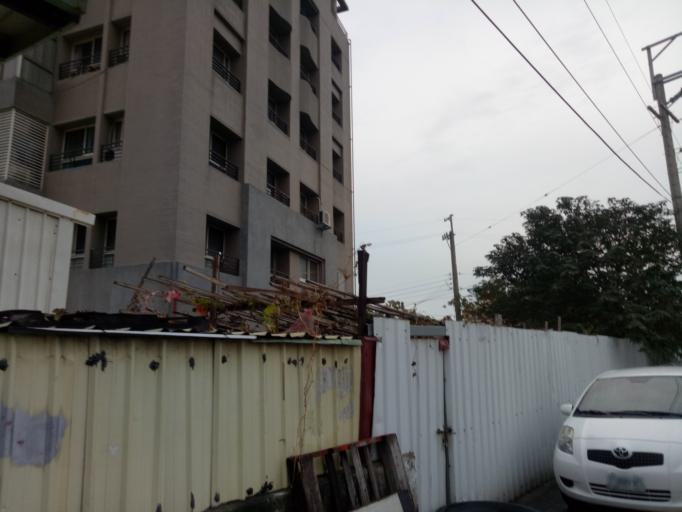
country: TW
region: Taiwan
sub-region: Taichung City
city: Taichung
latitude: 24.2464
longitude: 120.5413
